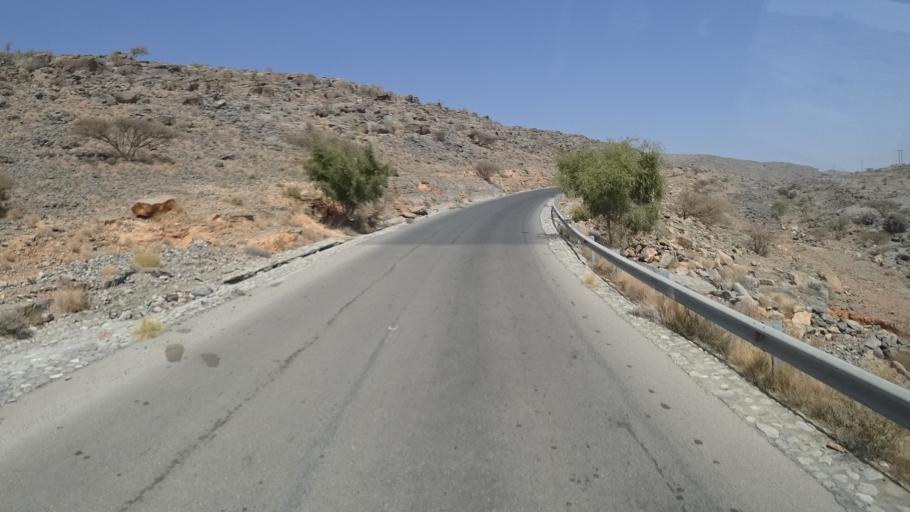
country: OM
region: Muhafazat ad Dakhiliyah
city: Bahla'
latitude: 23.0996
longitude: 57.3924
